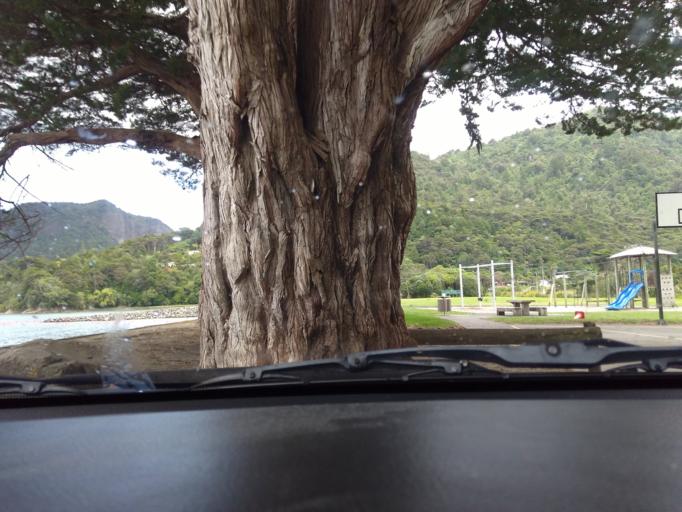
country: NZ
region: Auckland
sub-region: Auckland
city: Titirangi
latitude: -36.9994
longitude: 174.5704
